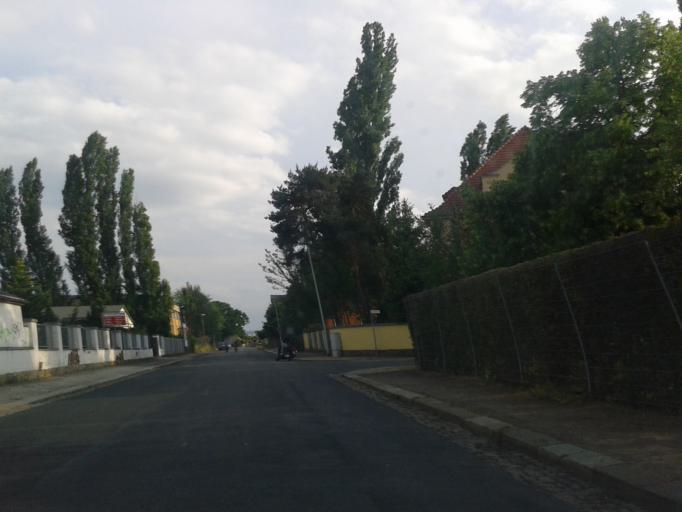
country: DE
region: Saxony
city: Radebeul
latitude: 51.0933
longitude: 13.6913
